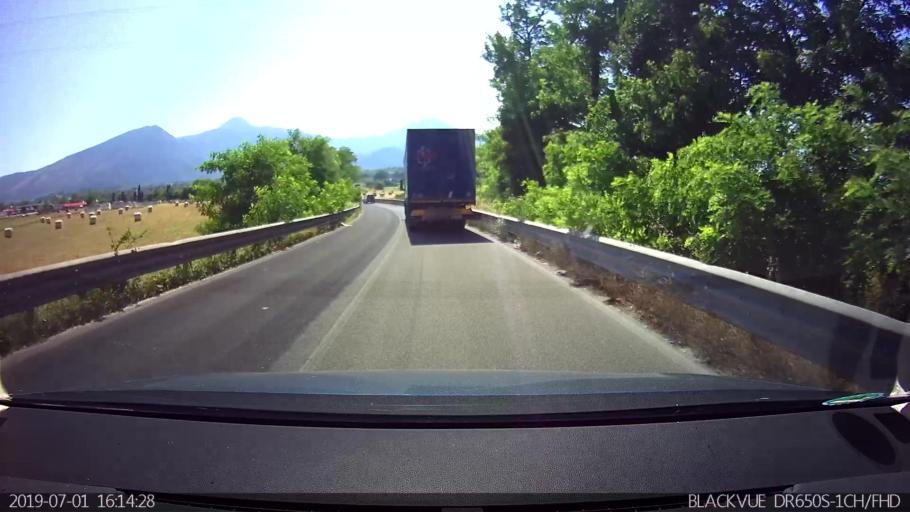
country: IT
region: Latium
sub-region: Provincia di Frosinone
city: Ceccano
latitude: 41.6010
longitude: 13.2958
